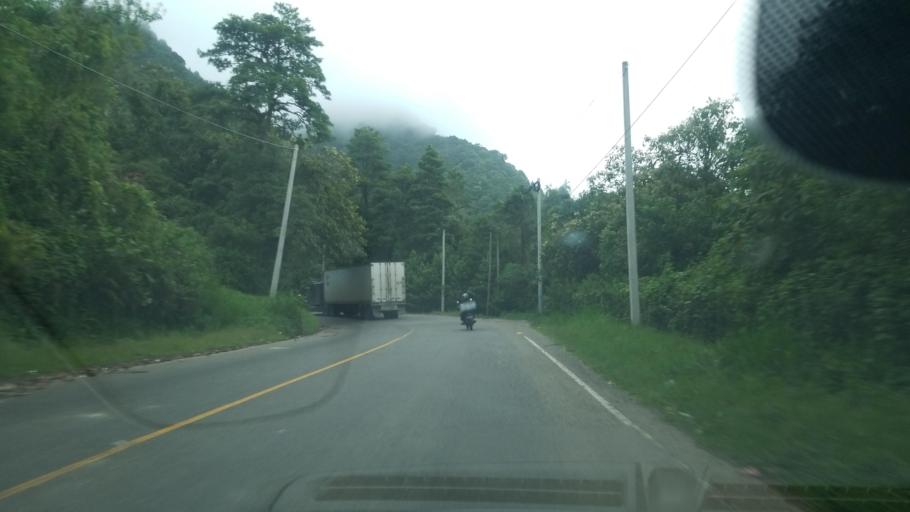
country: HN
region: Ocotepeque
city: La Labor
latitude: 14.4750
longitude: -89.0585
